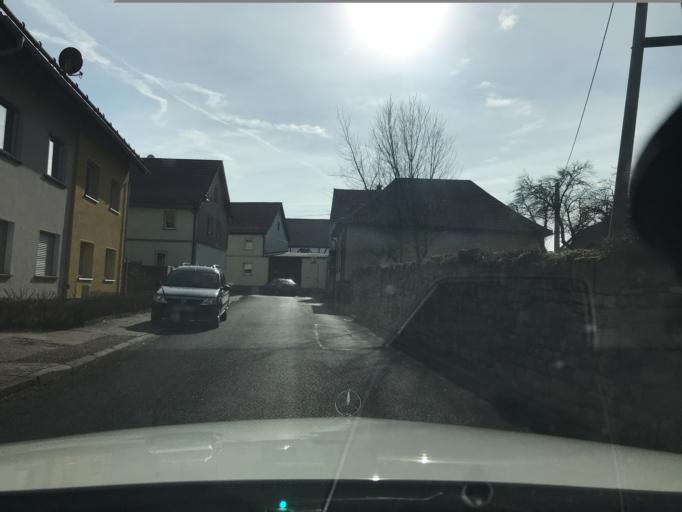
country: DE
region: Thuringia
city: Ernstroda
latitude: 50.9013
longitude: 10.6309
